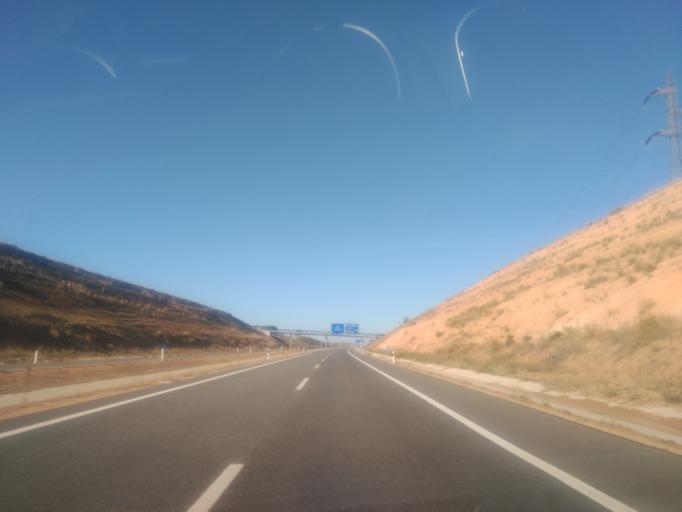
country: ES
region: Castille and Leon
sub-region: Provincia de Burgos
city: Fuentespina
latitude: 41.6397
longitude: -3.6689
